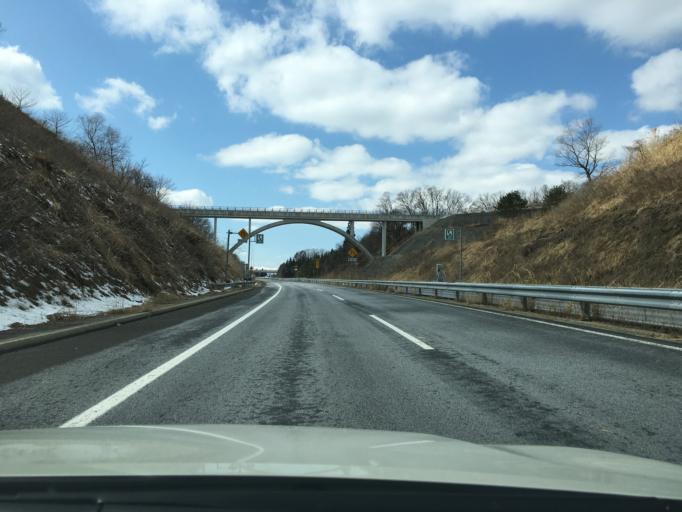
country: JP
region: Yamagata
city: Sagae
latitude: 38.4265
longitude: 140.1588
